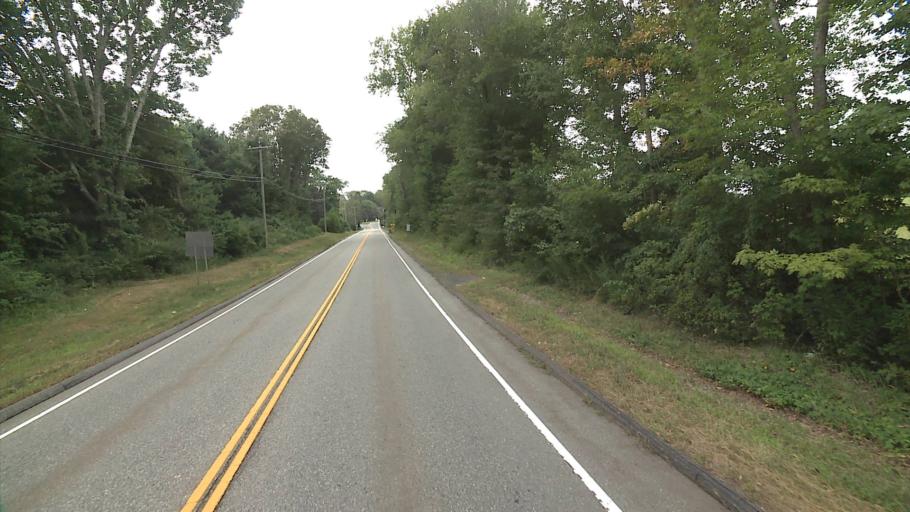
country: US
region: Connecticut
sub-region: Hartford County
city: Terramuggus
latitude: 41.6952
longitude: -72.4373
